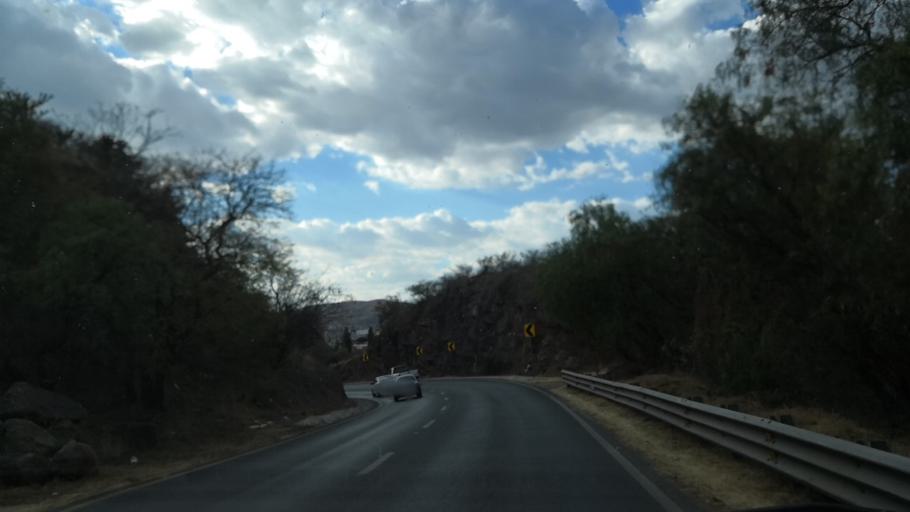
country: MX
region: Guanajuato
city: Marfil
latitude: 21.0035
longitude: -101.2796
